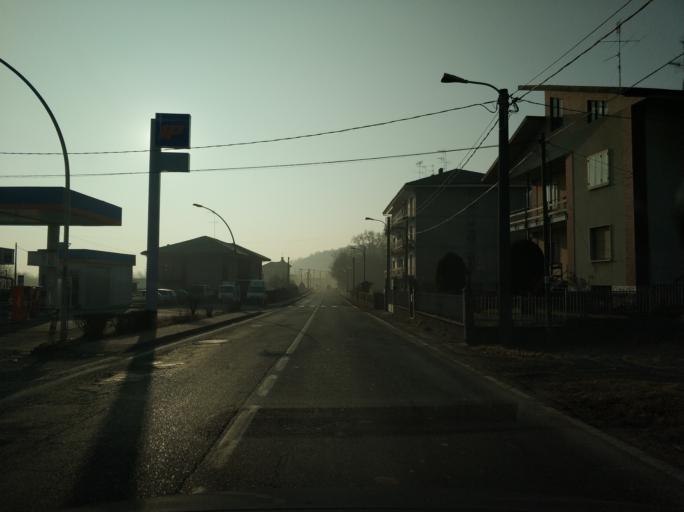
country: IT
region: Piedmont
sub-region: Provincia di Torino
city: Front
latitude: 45.2781
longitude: 7.6662
